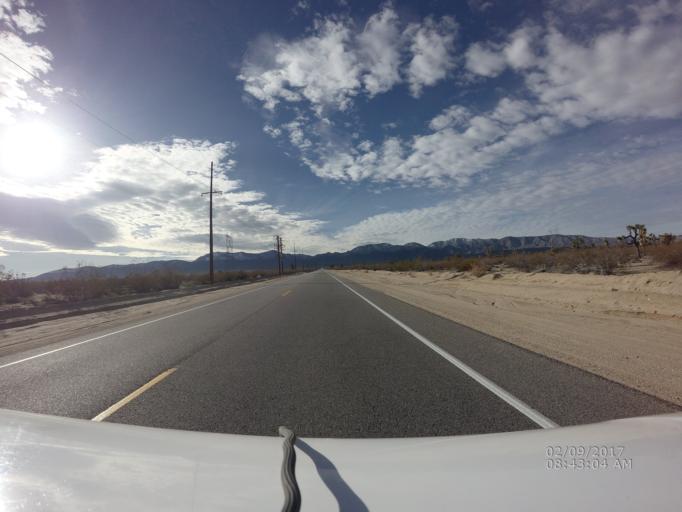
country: US
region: California
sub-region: Los Angeles County
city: Lake Los Angeles
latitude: 34.5152
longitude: -117.8355
